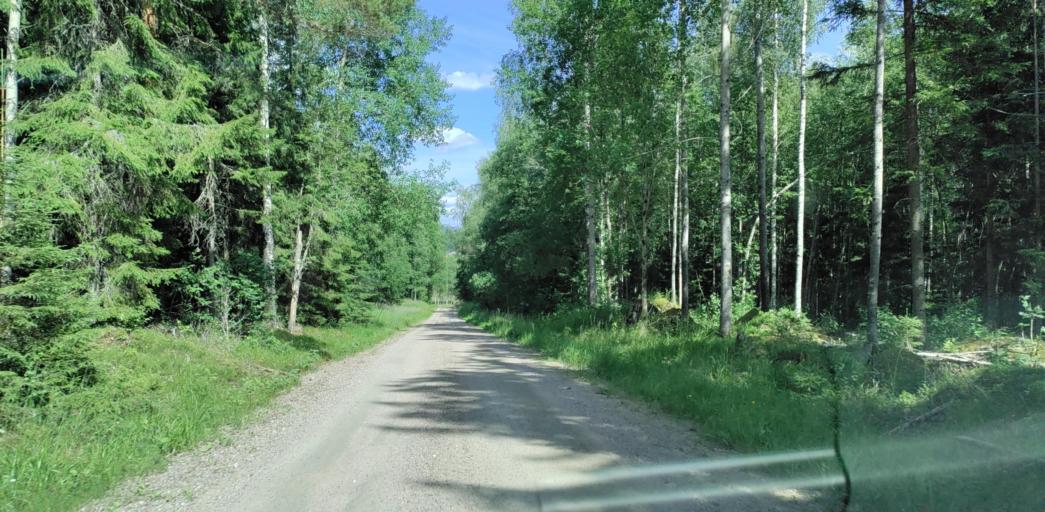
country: SE
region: Vaermland
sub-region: Hagfors Kommun
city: Ekshaerad
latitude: 60.0999
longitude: 13.4422
